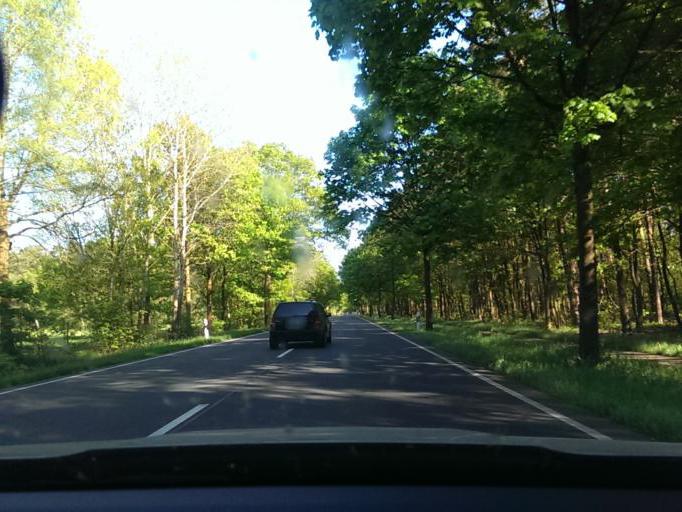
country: DE
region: Lower Saxony
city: Wietze
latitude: 52.6416
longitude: 9.8793
